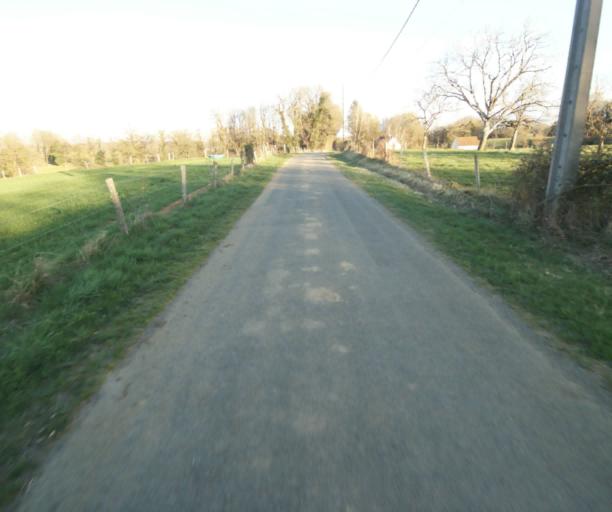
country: FR
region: Limousin
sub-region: Departement de la Correze
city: Uzerche
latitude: 45.3733
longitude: 1.5934
